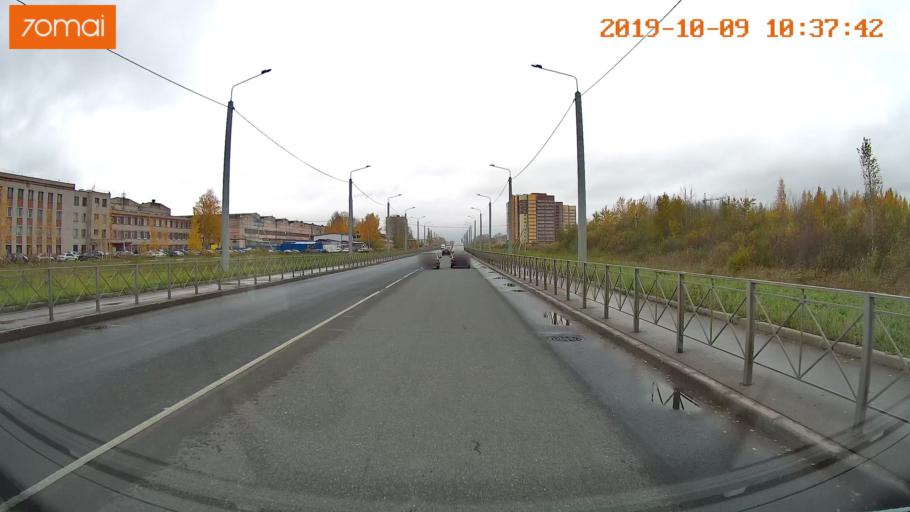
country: RU
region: Vologda
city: Vologda
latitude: 59.2355
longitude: 39.8573
